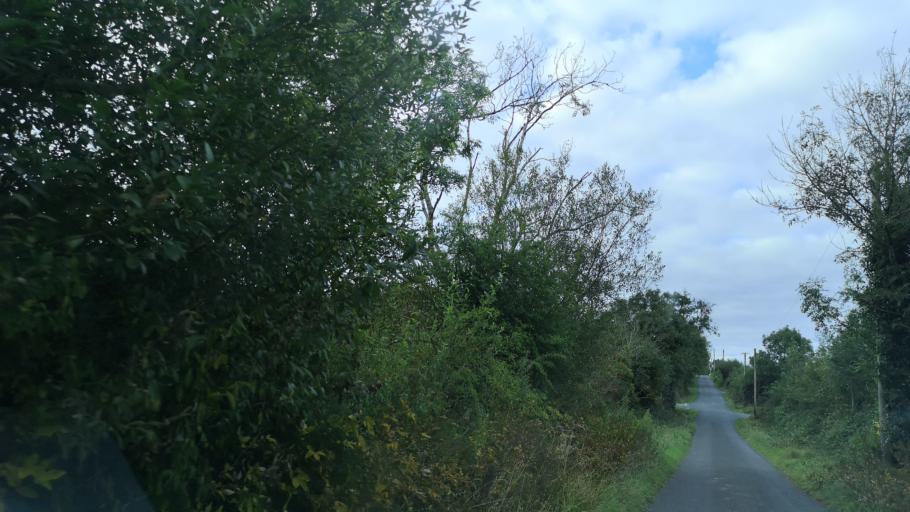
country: IE
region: Connaught
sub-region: County Galway
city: Loughrea
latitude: 53.1484
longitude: -8.5164
